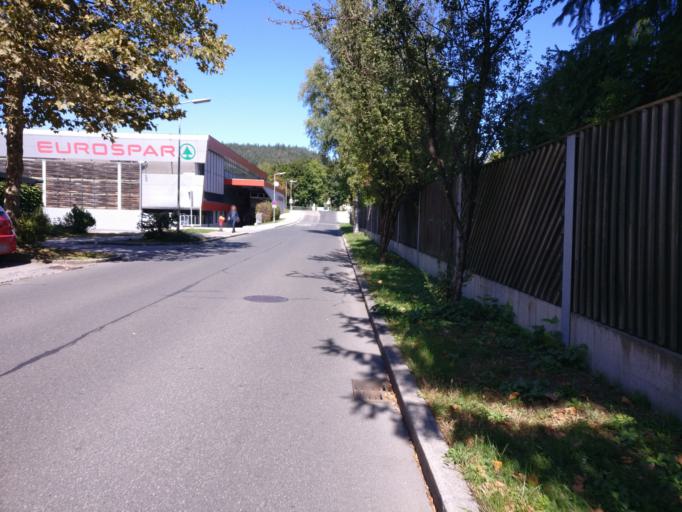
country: AT
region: Carinthia
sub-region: Klagenfurt am Woerthersee
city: Klagenfurt am Woerthersee
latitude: 46.6185
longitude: 14.2783
